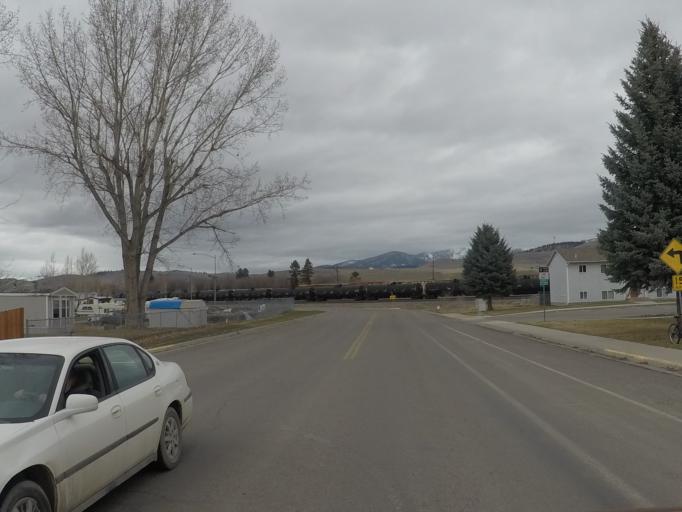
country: US
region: Montana
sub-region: Missoula County
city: Missoula
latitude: 46.8875
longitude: -114.0184
